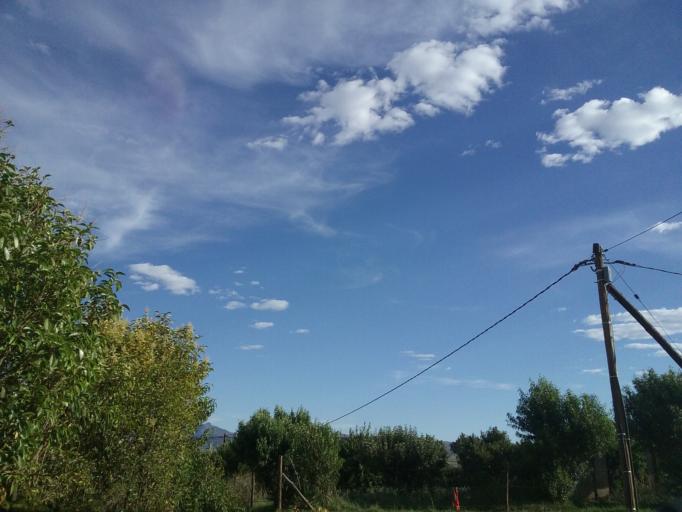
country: LS
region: Maseru
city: Maseru
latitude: -29.4311
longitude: 27.5716
